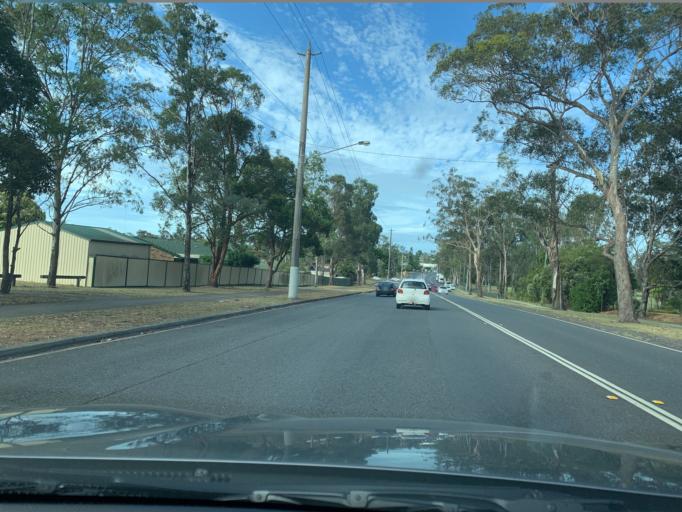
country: AU
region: Queensland
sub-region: Brisbane
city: Wynnum West
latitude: -27.4726
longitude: 153.1473
